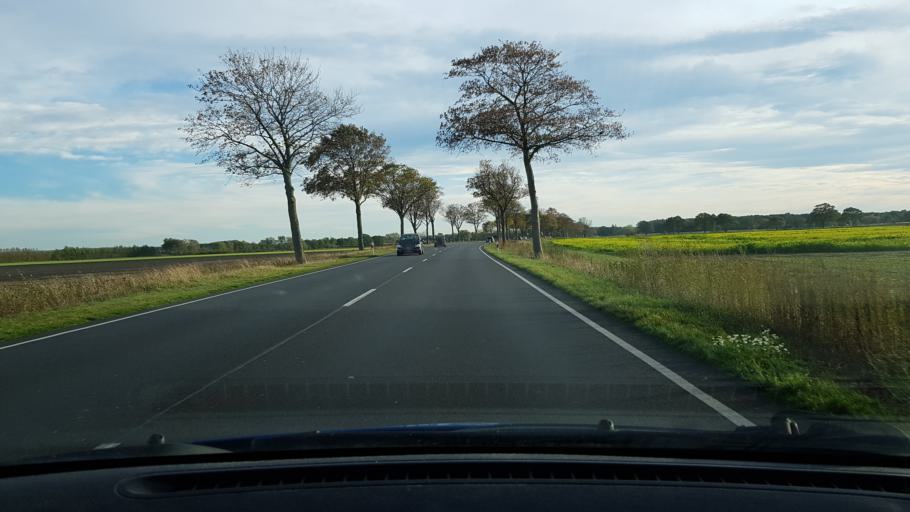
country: DE
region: Lower Saxony
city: Meine
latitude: 52.3693
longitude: 10.5383
